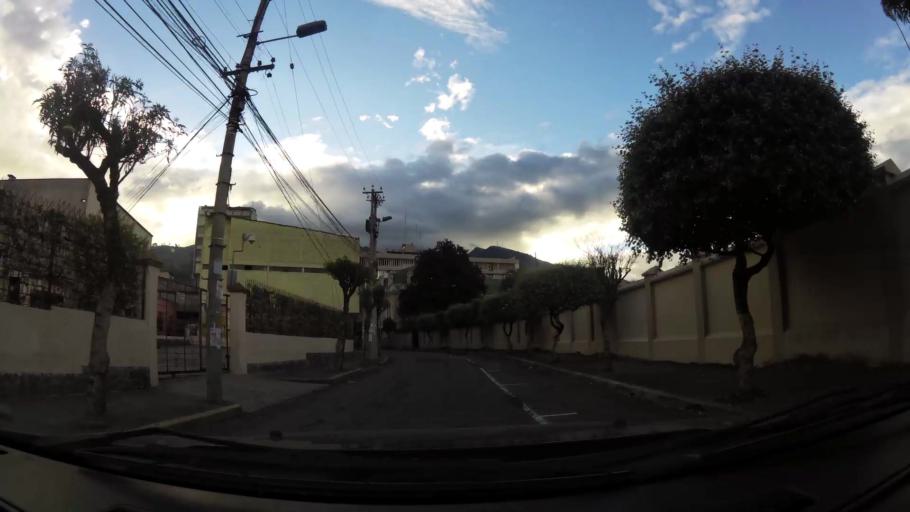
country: EC
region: Pichincha
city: Quito
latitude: -0.2034
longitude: -78.4970
